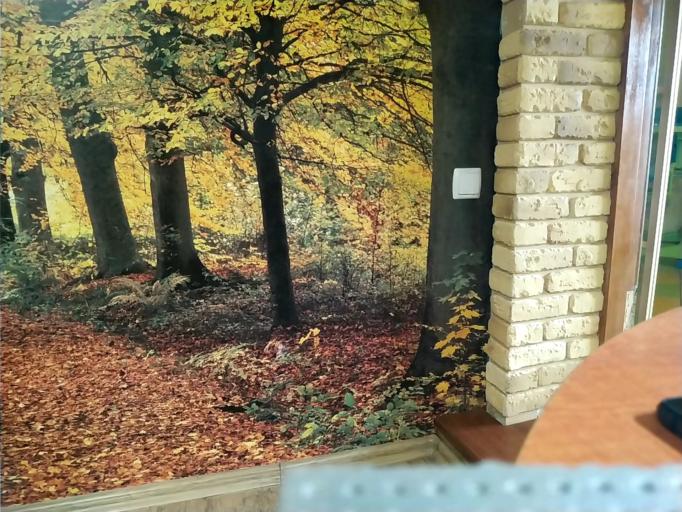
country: RU
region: Tverskaya
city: Kalashnikovo
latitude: 57.2734
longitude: 35.2226
